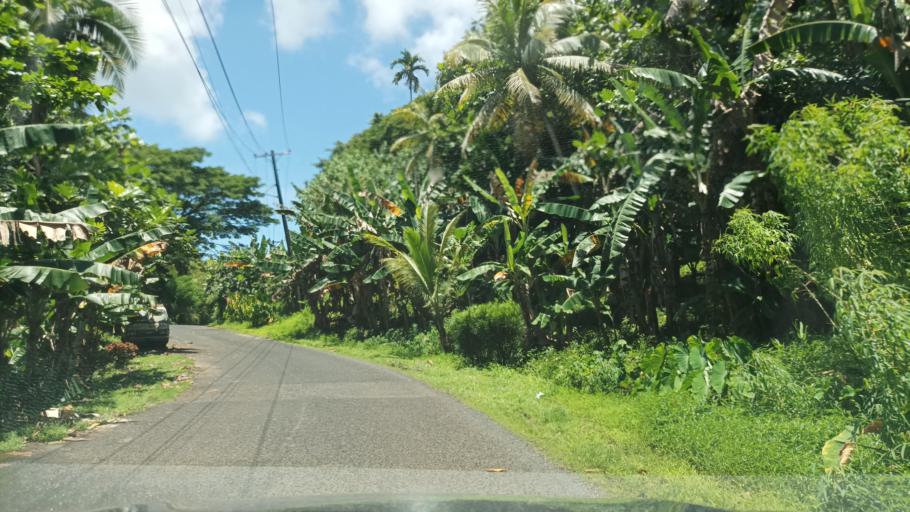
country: FM
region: Pohnpei
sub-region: Madolenihm Municipality
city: Madolenihm Municipality Government
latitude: 6.8541
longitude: 158.2963
